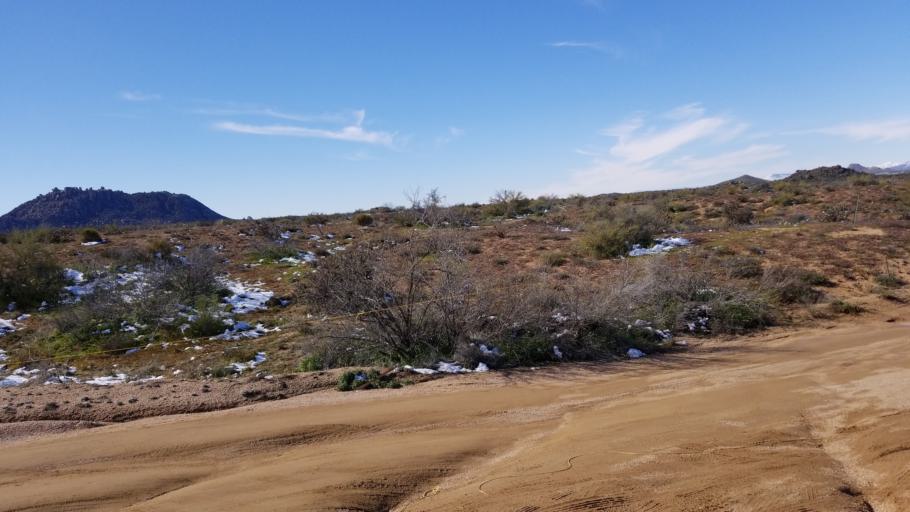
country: US
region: Arizona
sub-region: Maricopa County
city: Rio Verde
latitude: 33.7138
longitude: -111.8047
